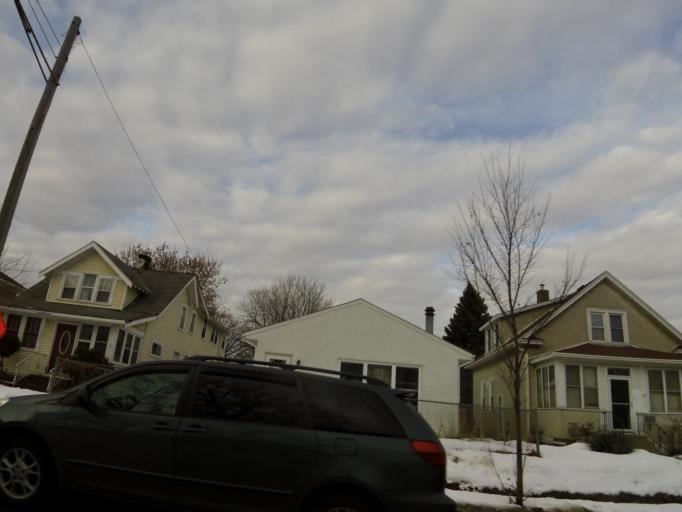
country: US
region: Minnesota
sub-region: Ramsey County
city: Maplewood
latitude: 44.9668
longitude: -93.0266
